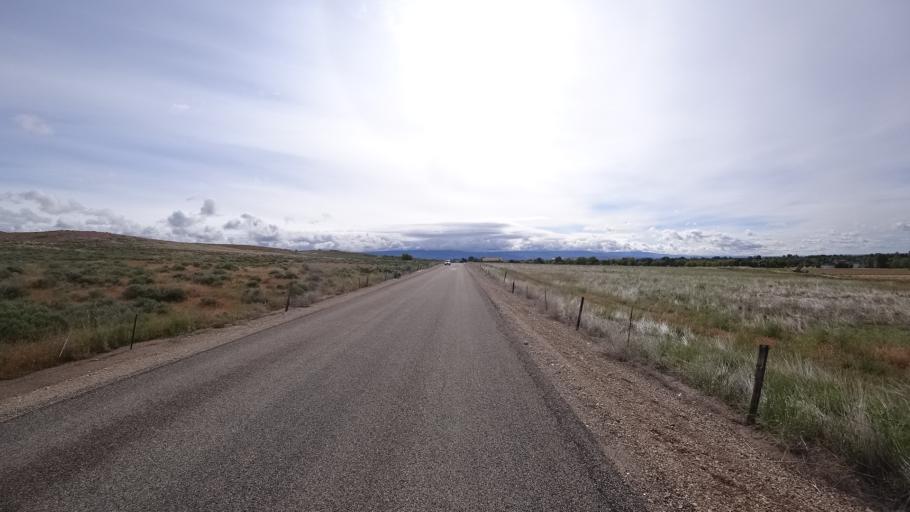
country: US
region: Idaho
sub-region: Ada County
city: Eagle
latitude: 43.7355
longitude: -116.4114
